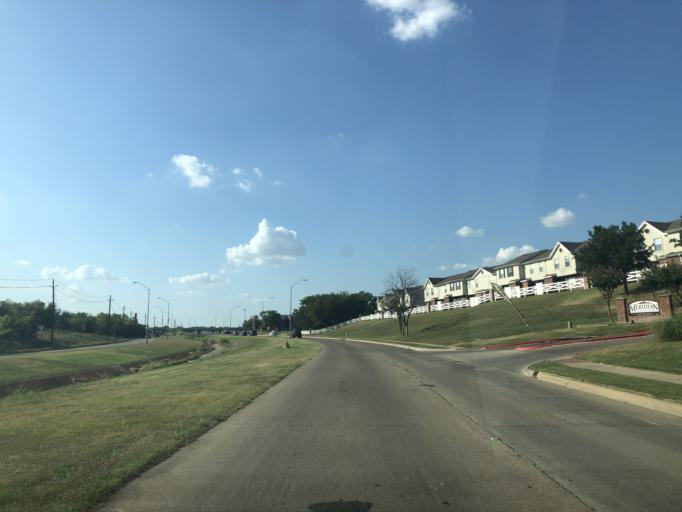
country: US
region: Texas
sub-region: Tarrant County
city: Sansom Park
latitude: 32.8207
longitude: -97.3835
